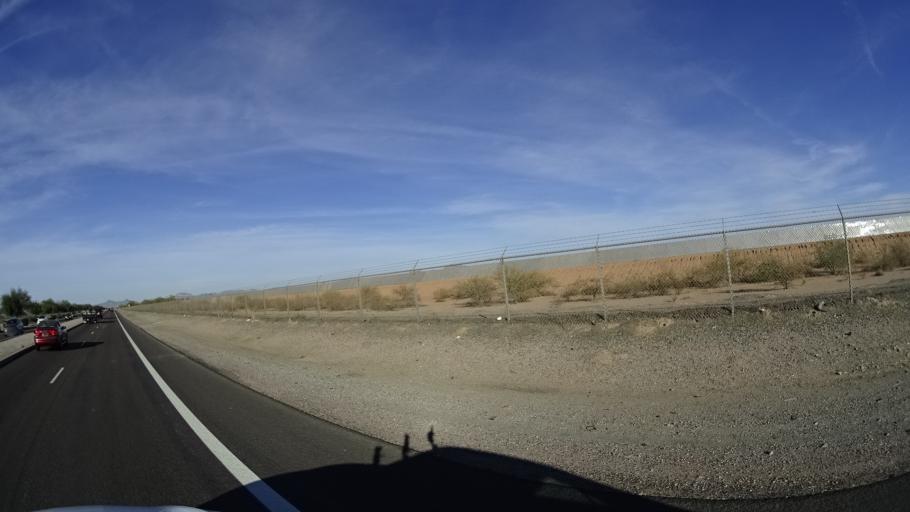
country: US
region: Arizona
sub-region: Maricopa County
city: Queen Creek
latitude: 33.2970
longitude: -111.6349
